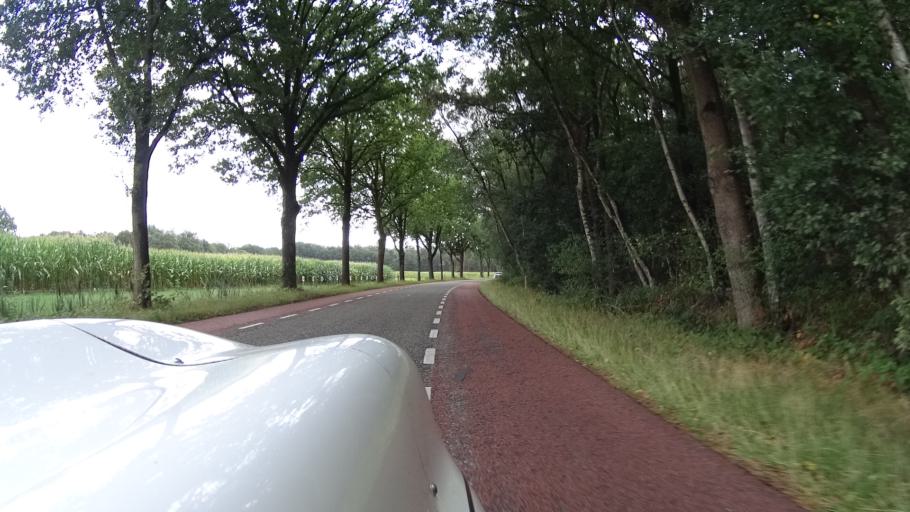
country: NL
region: North Brabant
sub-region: Gemeente Bernheze
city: Loosbroek
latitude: 51.6763
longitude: 5.4635
